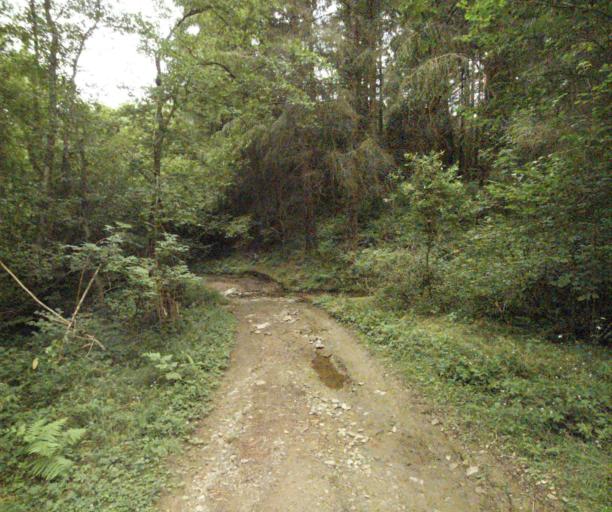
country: FR
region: Midi-Pyrenees
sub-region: Departement du Tarn
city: Soreze
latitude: 43.4197
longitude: 2.1119
